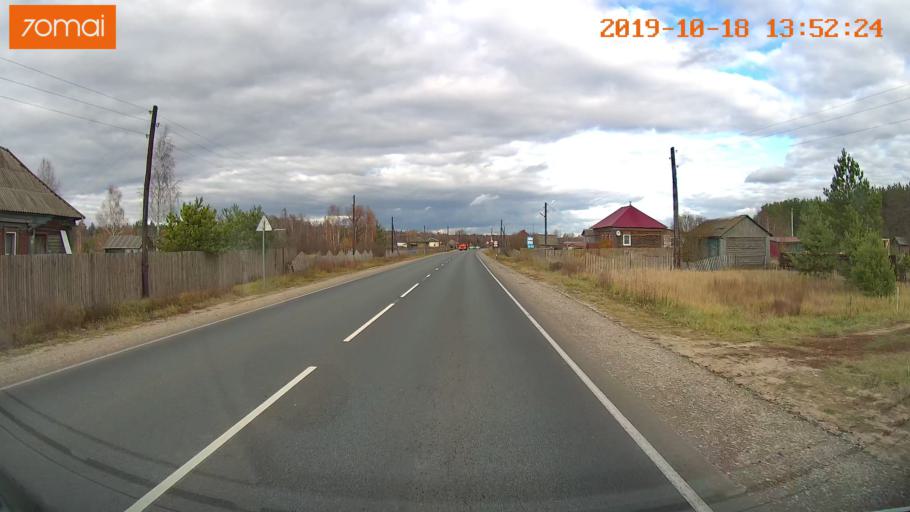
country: RU
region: Moskovskaya
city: Radovitskiy
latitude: 55.0297
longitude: 39.9679
